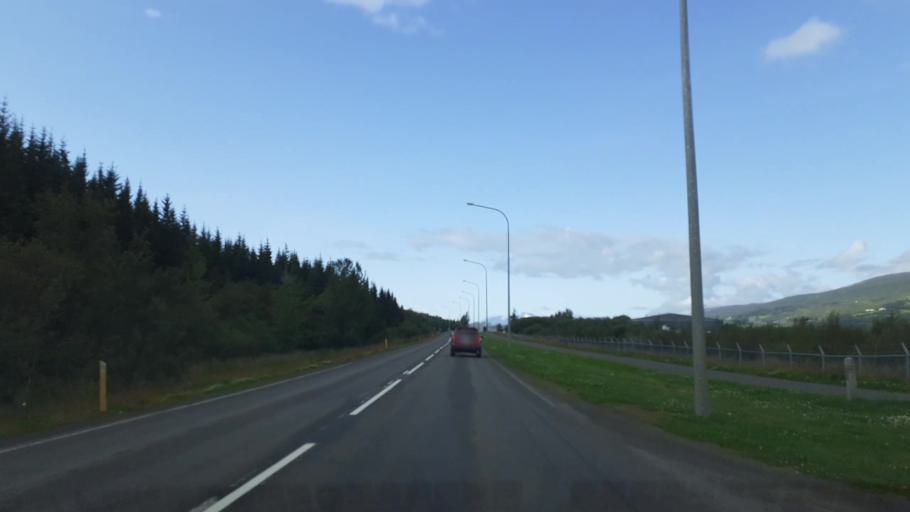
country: IS
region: Northeast
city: Akureyri
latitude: 65.6487
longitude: -18.0760
